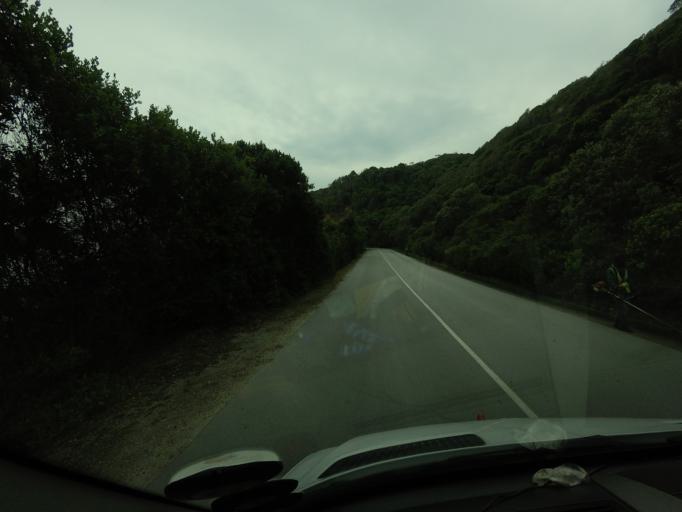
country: ZA
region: Eastern Cape
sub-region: Cacadu District Municipality
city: Kareedouw
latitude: -34.0215
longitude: 23.8840
